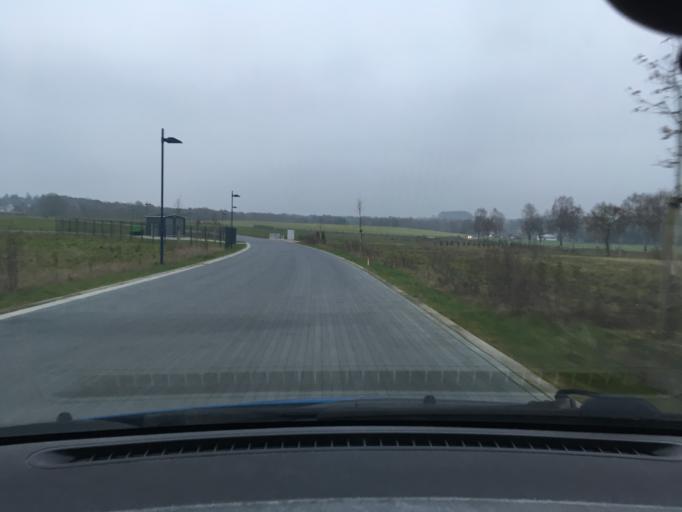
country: DE
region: Lower Saxony
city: Bispingen
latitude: 53.0983
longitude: 9.9821
